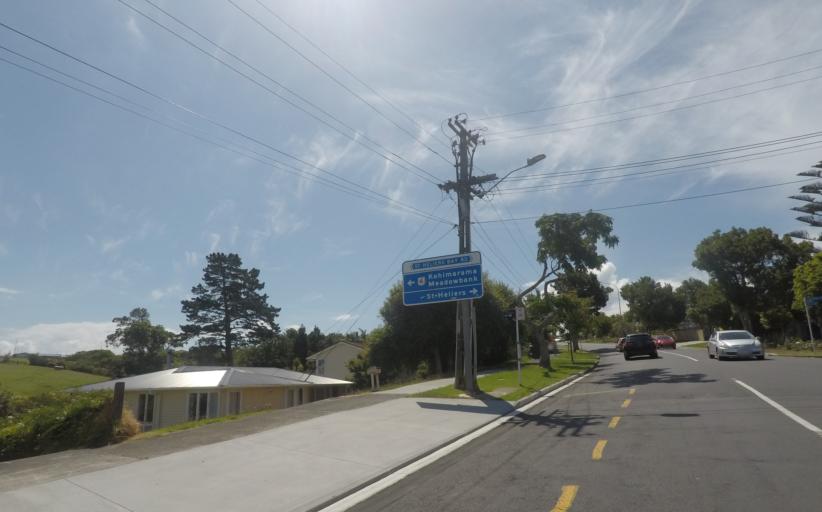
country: NZ
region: Auckland
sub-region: Auckland
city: Tamaki
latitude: -36.8691
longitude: 174.8493
